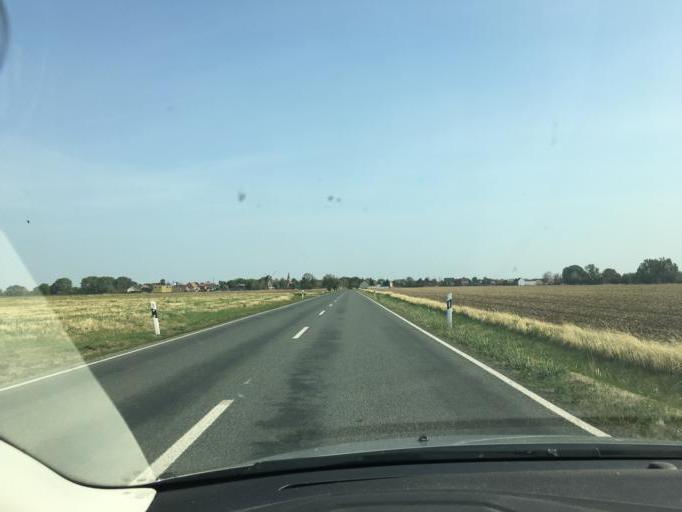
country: DE
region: Saxony-Anhalt
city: Plotzky
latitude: 51.9978
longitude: 11.8236
